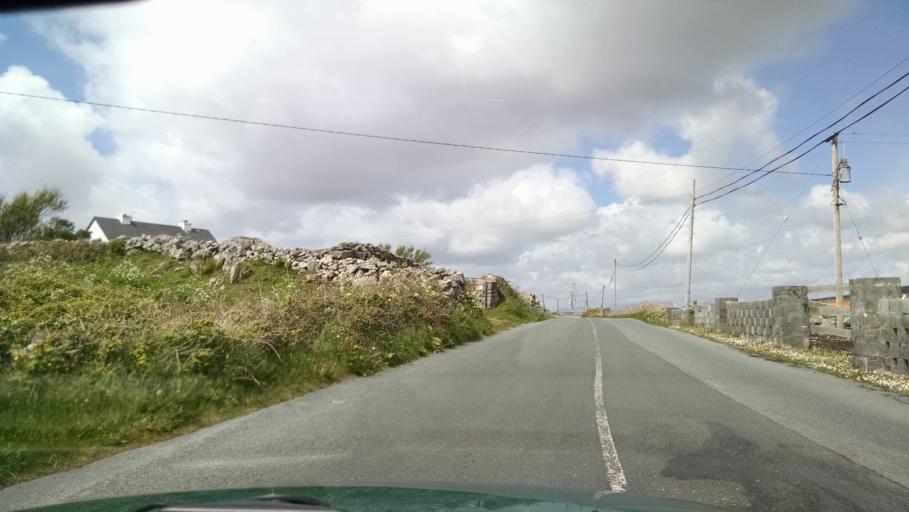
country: IE
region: Connaught
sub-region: County Galway
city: Clifden
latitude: 53.3065
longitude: -9.7815
